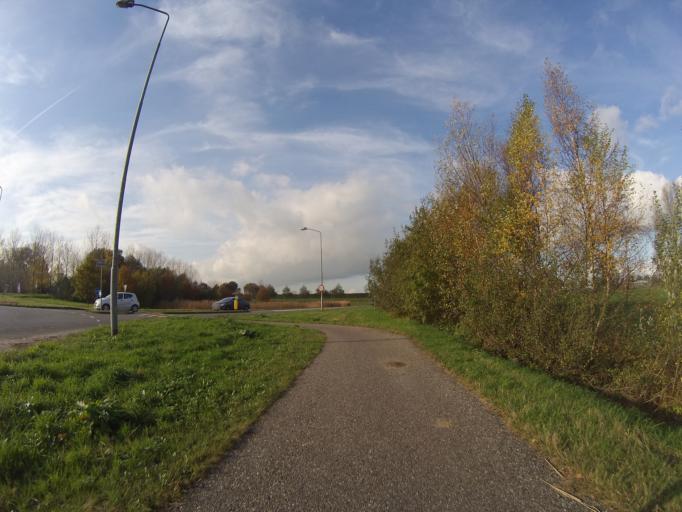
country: NL
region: Gelderland
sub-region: Gemeente Nijkerk
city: Nijkerk
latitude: 52.2219
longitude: 5.4570
